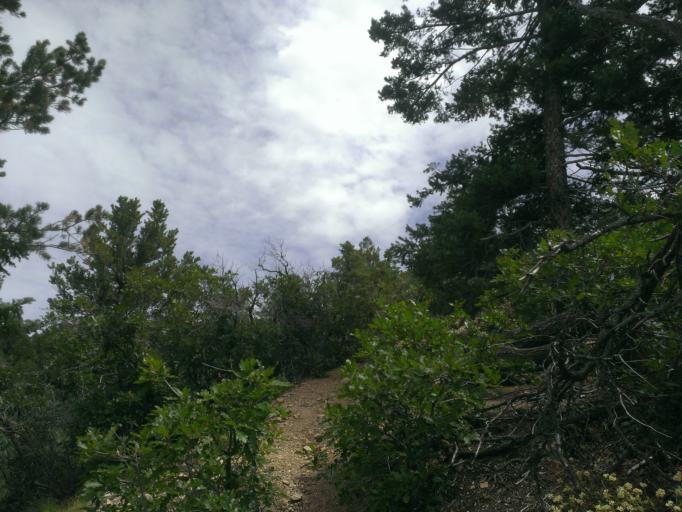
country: US
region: New Mexico
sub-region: Taos County
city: Arroyo Seco
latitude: 36.5374
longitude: -105.5541
